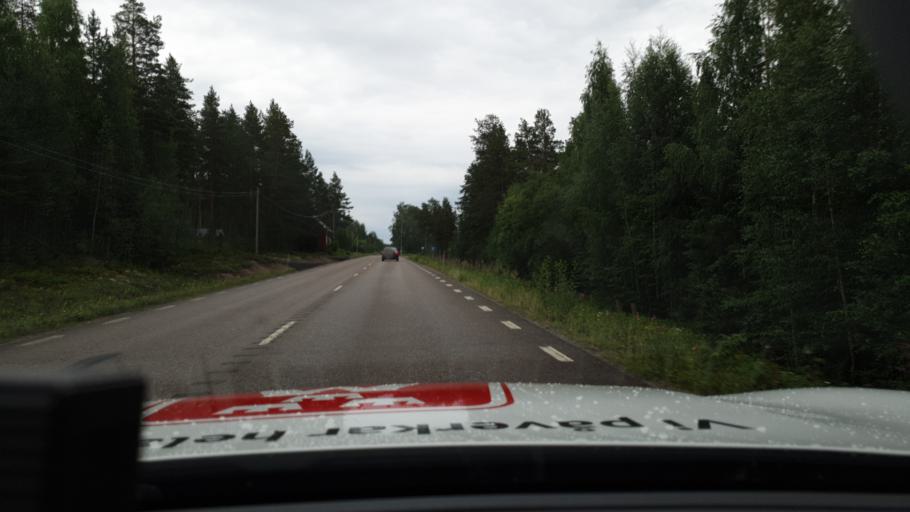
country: SE
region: Norrbotten
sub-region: Alvsbyns Kommun
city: AElvsbyn
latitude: 66.1123
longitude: 20.9296
